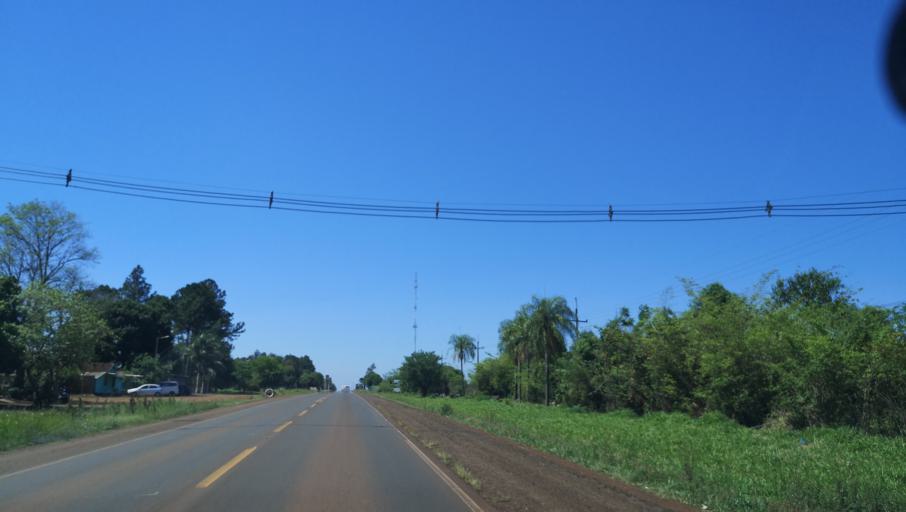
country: PY
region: Itapua
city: San Juan del Parana
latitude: -27.2625
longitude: -55.9636
